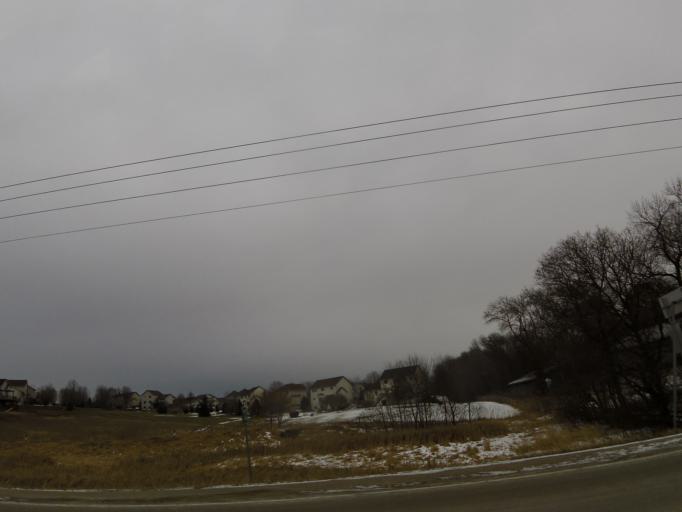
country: US
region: Minnesota
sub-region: Carver County
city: Waconia
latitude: 44.8260
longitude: -93.7884
